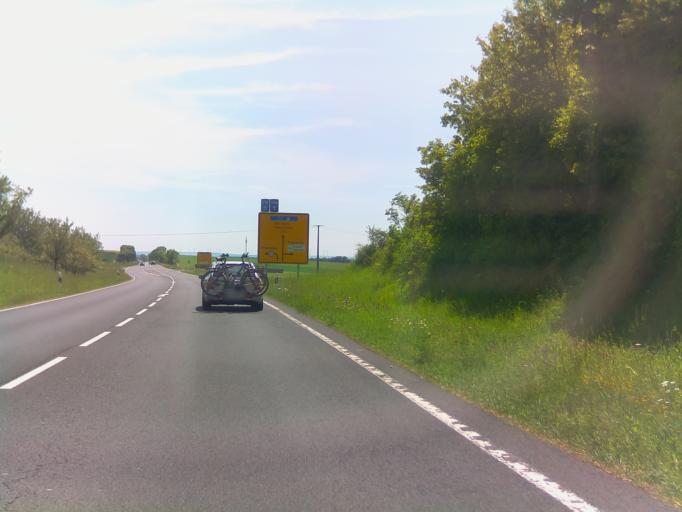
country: DE
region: Bavaria
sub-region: Regierungsbezirk Unterfranken
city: Oerlenbach
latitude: 50.1644
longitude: 10.1483
